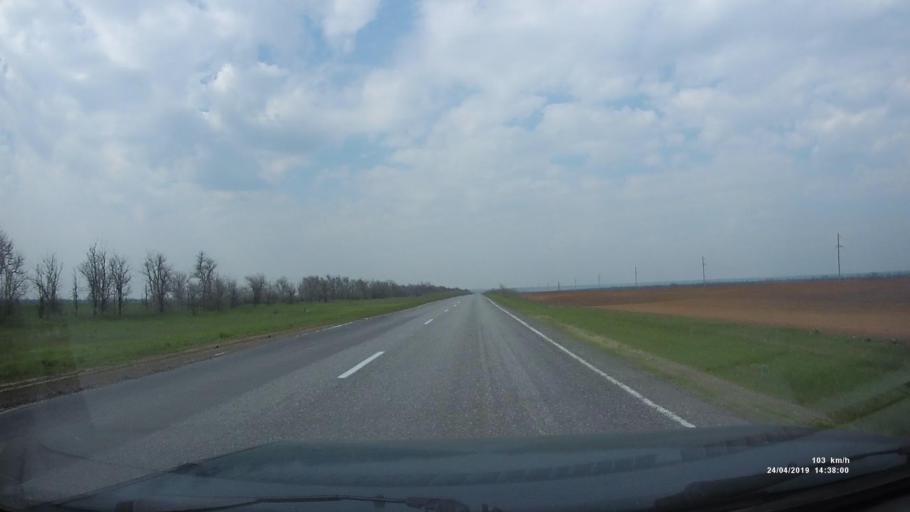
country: RU
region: Rostov
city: Remontnoye
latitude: 46.3945
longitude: 43.8863
